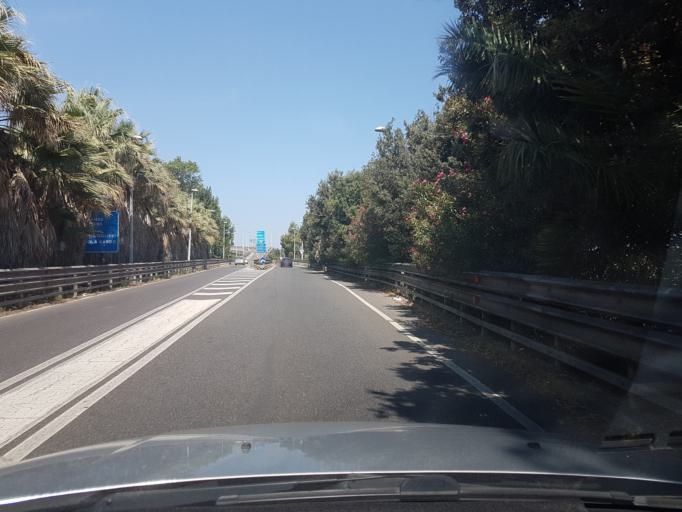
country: IT
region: Sardinia
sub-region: Provincia di Oristano
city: Donigala Fenugheddu
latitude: 39.9246
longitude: 8.5802
